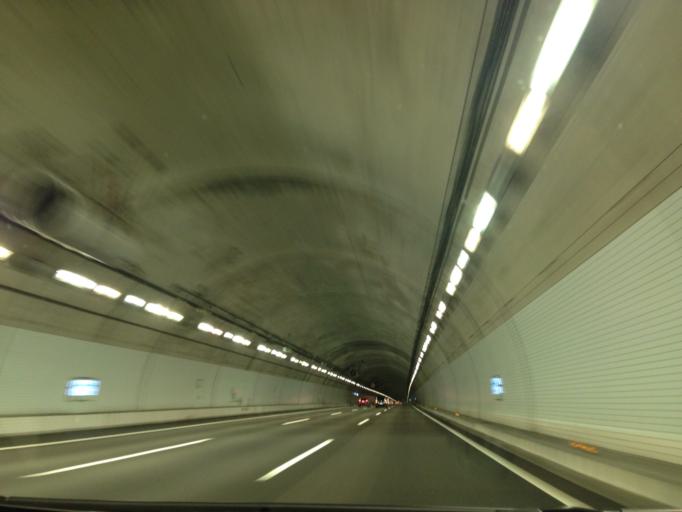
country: JP
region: Shizuoka
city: Shizuoka-shi
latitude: 34.9628
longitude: 138.2900
